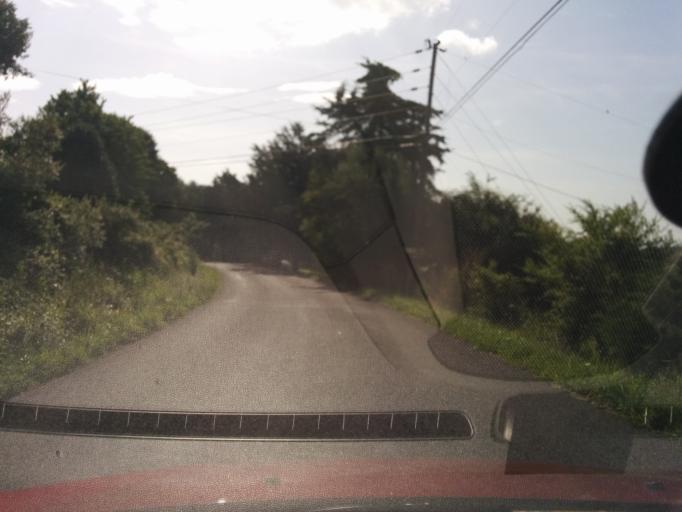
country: US
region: Virginia
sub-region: City of Lexington
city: Lexington
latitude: 37.7723
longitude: -79.4749
